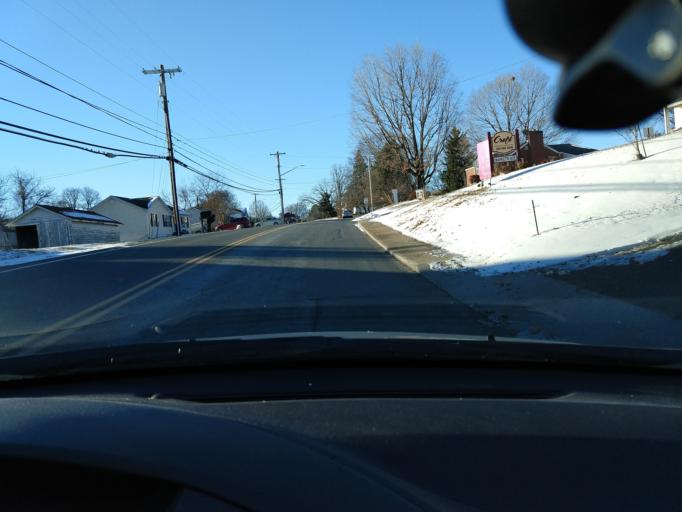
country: US
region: Virginia
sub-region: City of Bedford
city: Bedford
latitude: 37.3288
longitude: -79.5284
